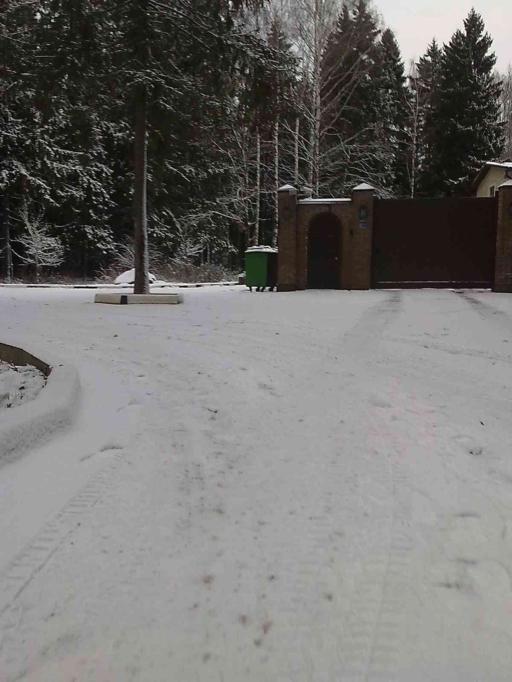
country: RU
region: Moskovskaya
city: Lesnoy Gorodok
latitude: 55.6553
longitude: 37.1581
